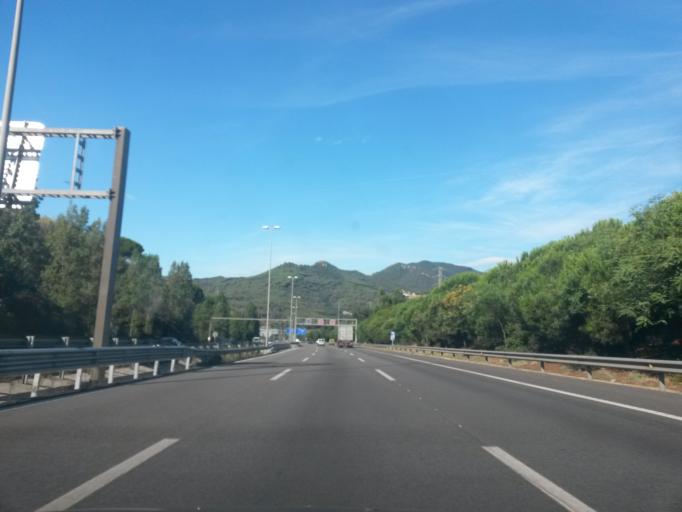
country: ES
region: Catalonia
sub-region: Provincia de Barcelona
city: Argentona
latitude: 41.5501
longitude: 2.4232
